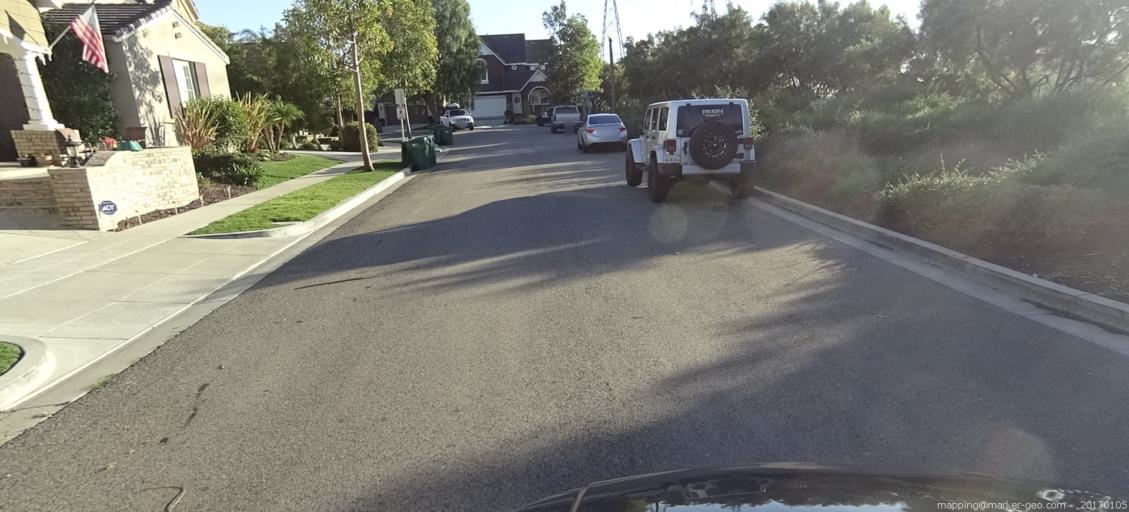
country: US
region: California
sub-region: Orange County
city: Ladera Ranch
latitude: 33.5489
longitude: -117.6418
